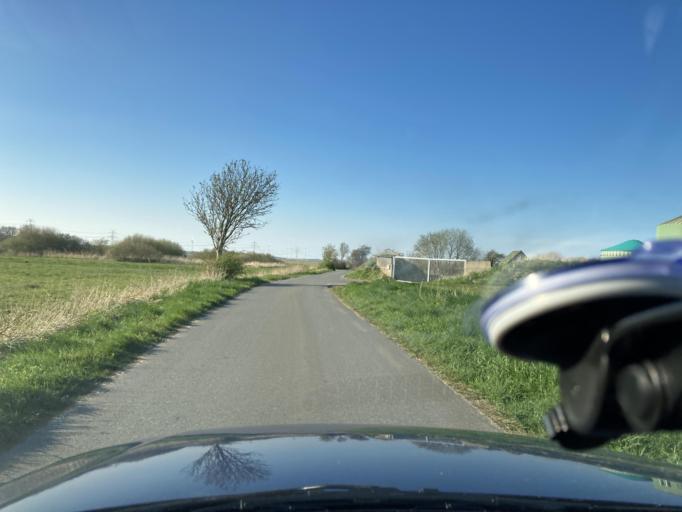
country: DE
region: Schleswig-Holstein
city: Lohe-Rickelshof
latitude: 54.1957
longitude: 9.0588
